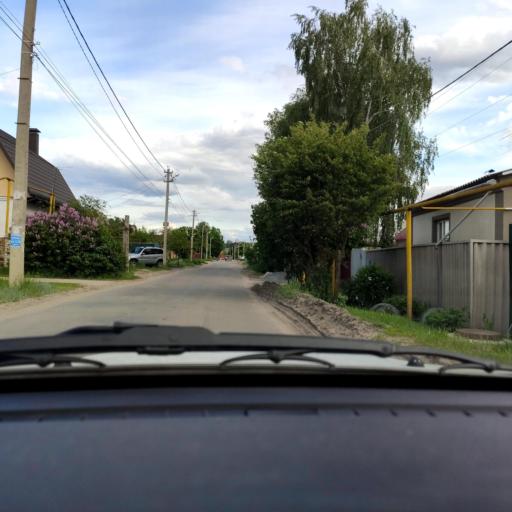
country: RU
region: Voronezj
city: Podgornoye
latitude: 51.7383
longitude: 39.1554
